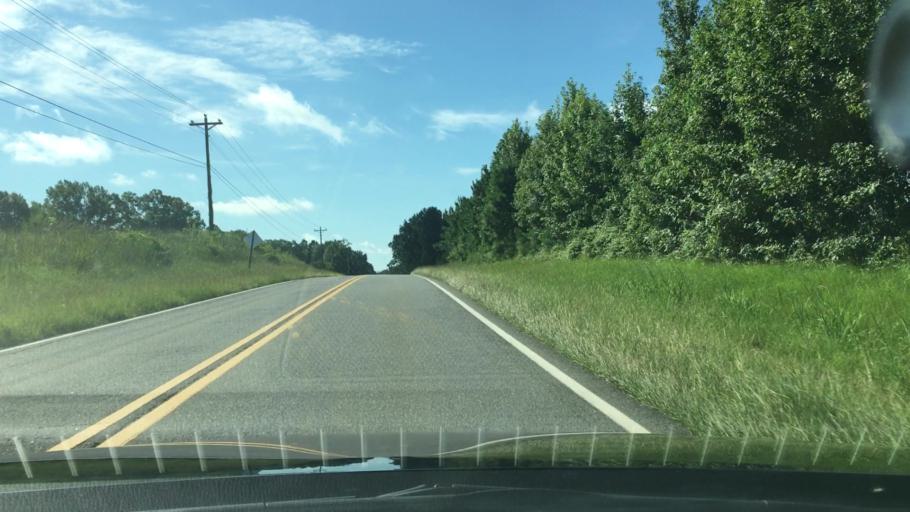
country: US
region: Georgia
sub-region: Putnam County
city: Jefferson
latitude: 33.4510
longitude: -83.2986
